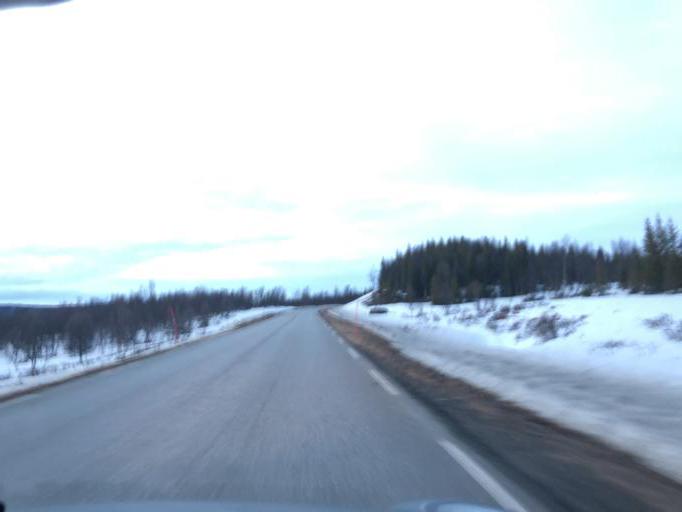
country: NO
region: Sor-Trondelag
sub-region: Tydal
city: Aas
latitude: 62.7177
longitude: 11.8196
